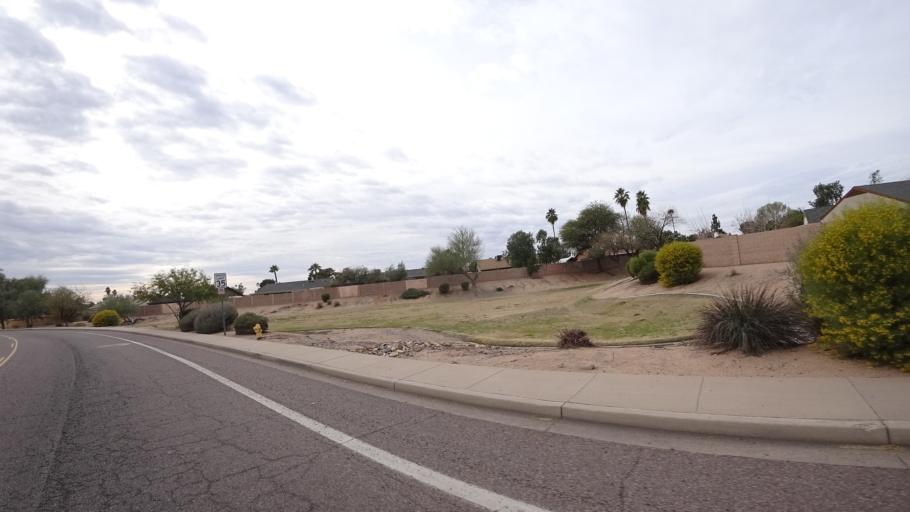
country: US
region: Arizona
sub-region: Maricopa County
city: Glendale
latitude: 33.6430
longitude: -112.1207
